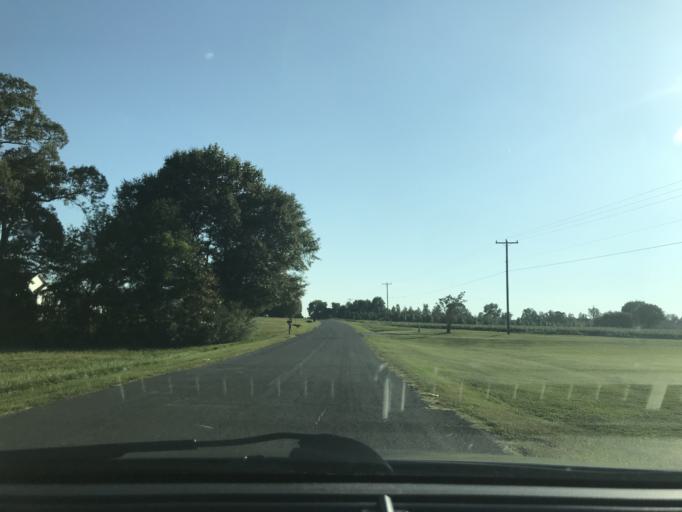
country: US
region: North Carolina
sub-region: Cleveland County
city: Boiling Springs
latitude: 35.1626
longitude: -81.7351
